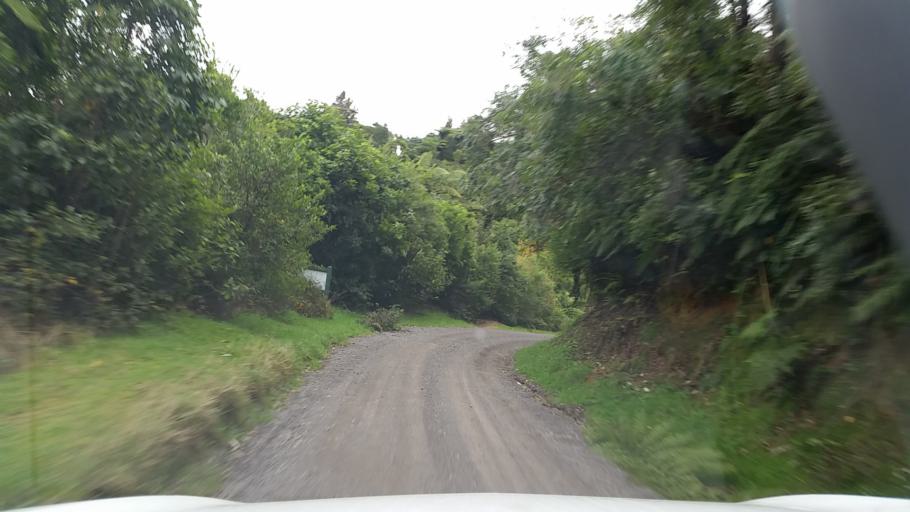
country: NZ
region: Bay of Plenty
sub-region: Rotorua District
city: Rotorua
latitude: -38.1589
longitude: 176.3621
